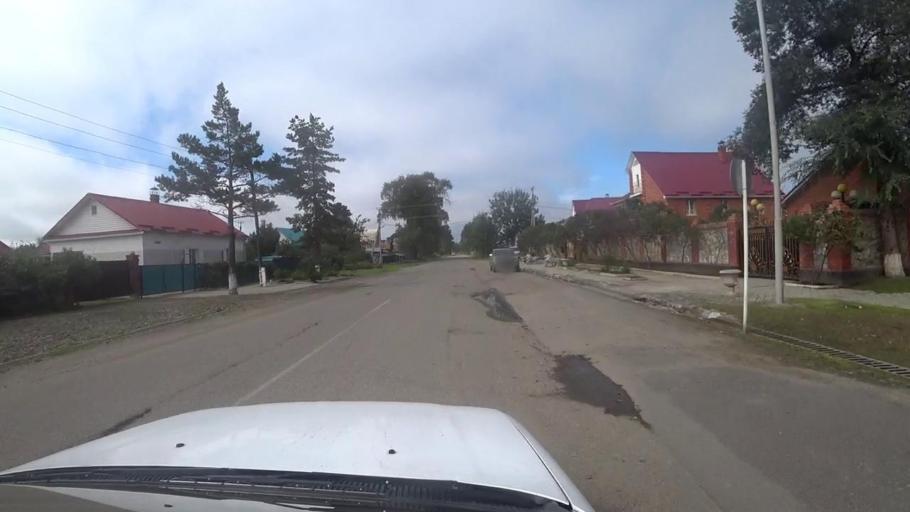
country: RU
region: Primorskiy
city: Dal'nerechensk
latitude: 45.9293
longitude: 133.7371
